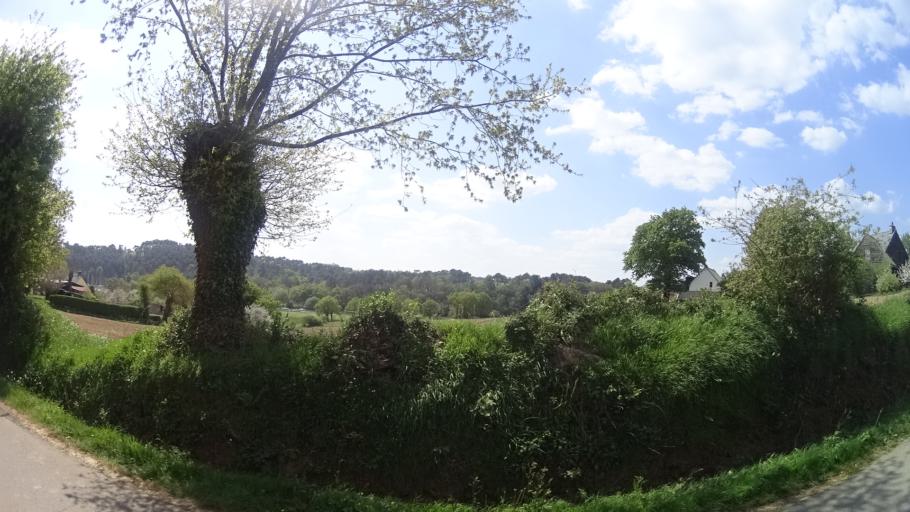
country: FR
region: Brittany
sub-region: Departement du Morbihan
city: Beganne
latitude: 47.5802
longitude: -2.2836
